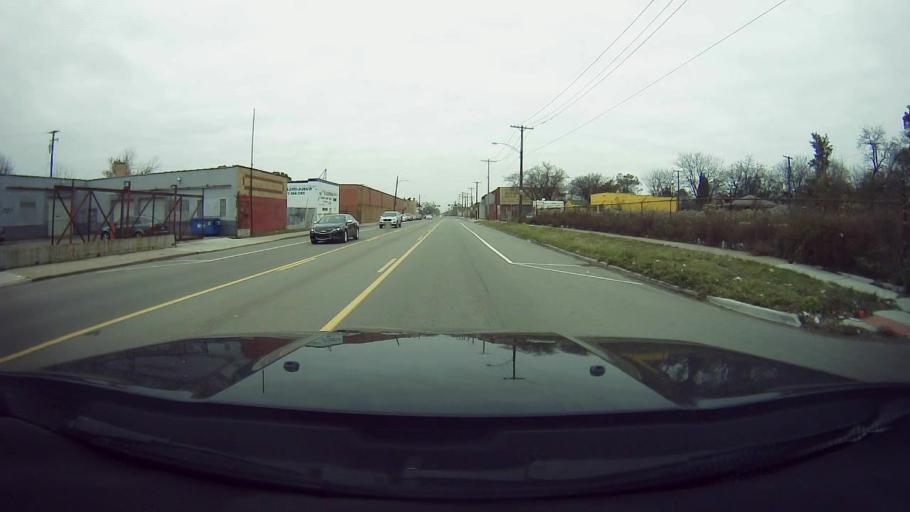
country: US
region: Michigan
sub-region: Wayne County
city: Hamtramck
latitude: 42.4200
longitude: -83.0645
